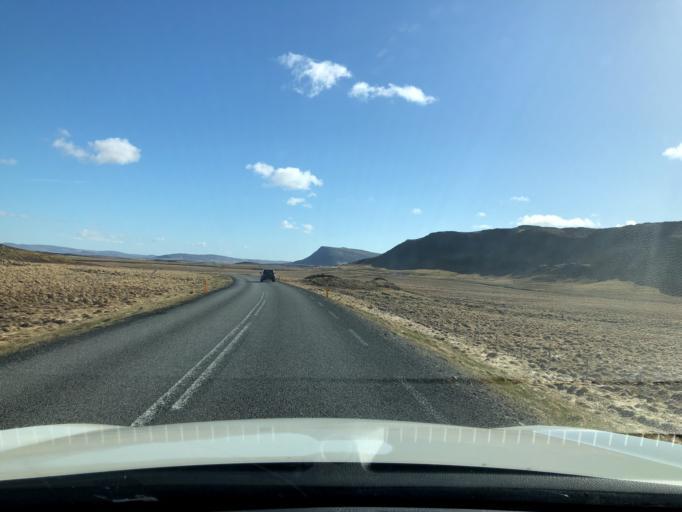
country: IS
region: West
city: Borgarnes
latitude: 64.5720
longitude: -21.6616
